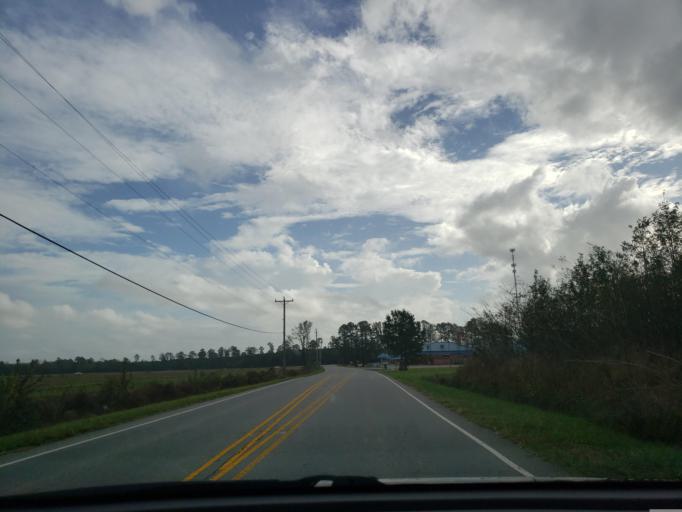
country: US
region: North Carolina
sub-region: Duplin County
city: Beulaville
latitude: 34.8271
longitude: -77.8120
